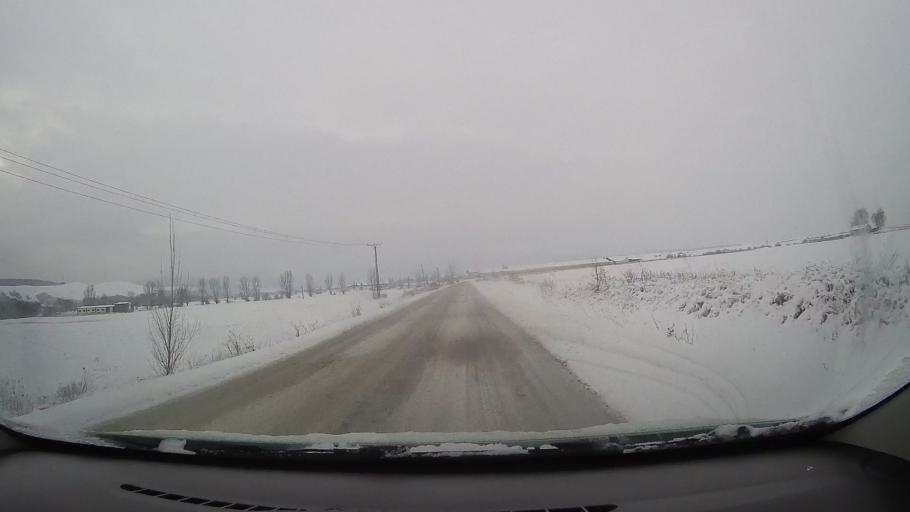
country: RO
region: Alba
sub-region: Comuna Pianu
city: Pianu de Jos
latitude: 45.9638
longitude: 23.4771
